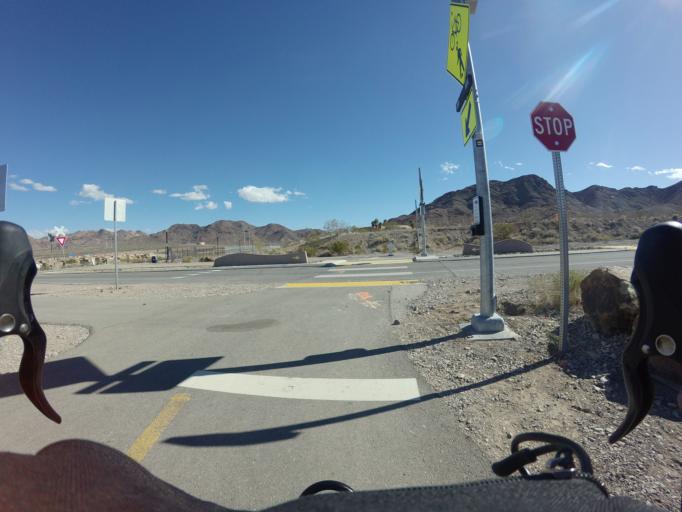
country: US
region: Nevada
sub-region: Clark County
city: Henderson
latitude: 35.9853
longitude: -114.9307
